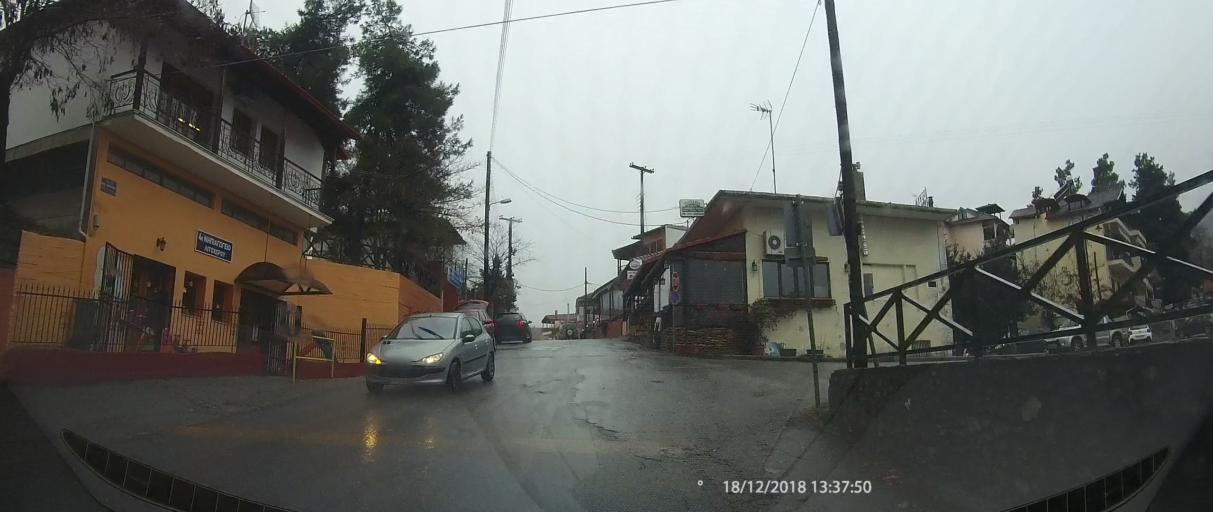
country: GR
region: Central Macedonia
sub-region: Nomos Pierias
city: Litochoro
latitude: 40.1060
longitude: 22.5027
